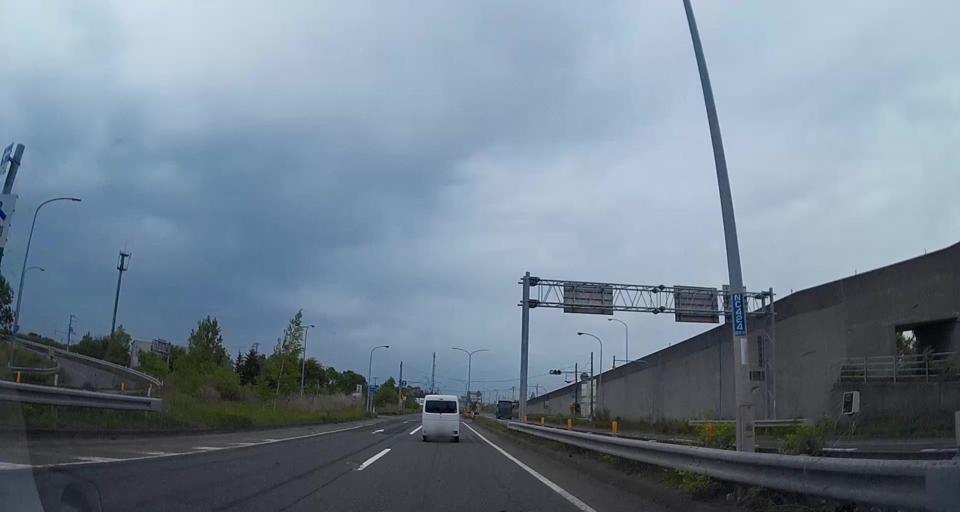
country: JP
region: Hokkaido
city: Tomakomai
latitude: 42.6774
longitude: 141.7115
